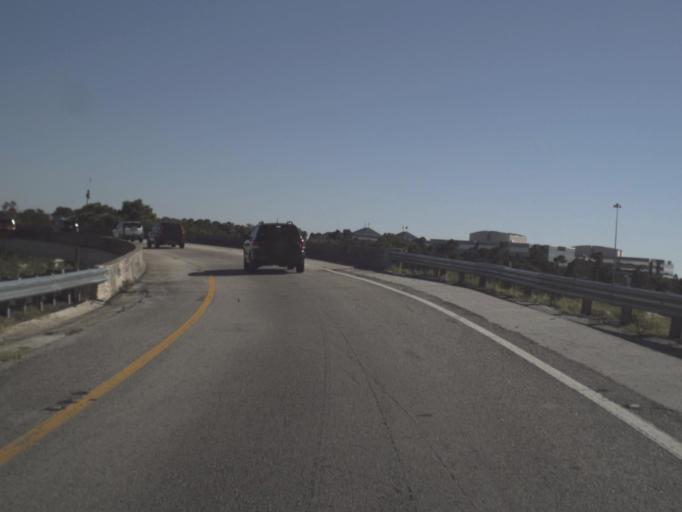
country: US
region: Florida
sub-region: Orange County
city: Williamsburg
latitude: 28.4207
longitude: -81.4749
